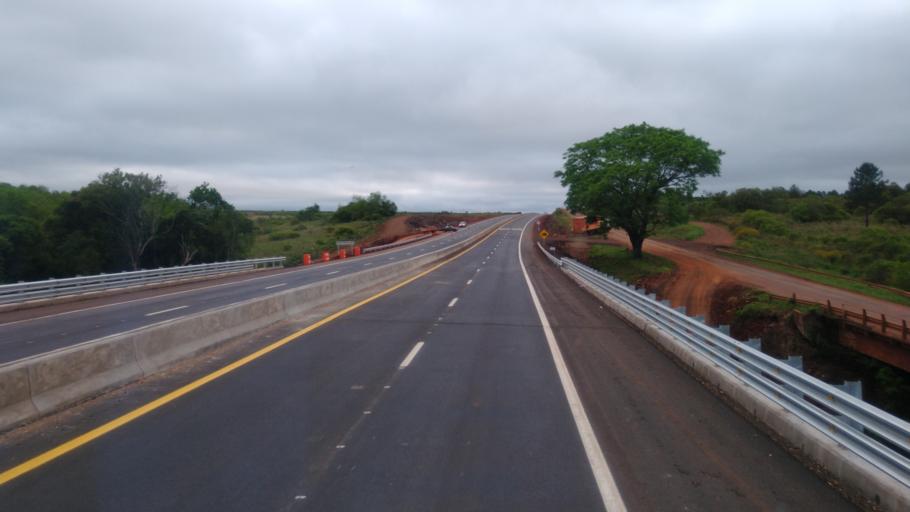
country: AR
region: Misiones
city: Cerro Cora
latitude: -27.4419
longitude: -55.6470
